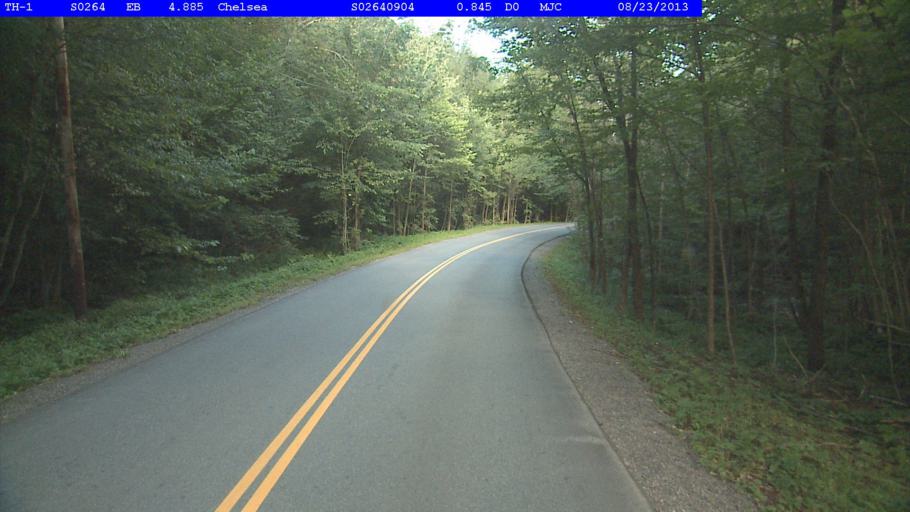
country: US
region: Vermont
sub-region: Orange County
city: Chelsea
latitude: 43.9713
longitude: -72.4965
